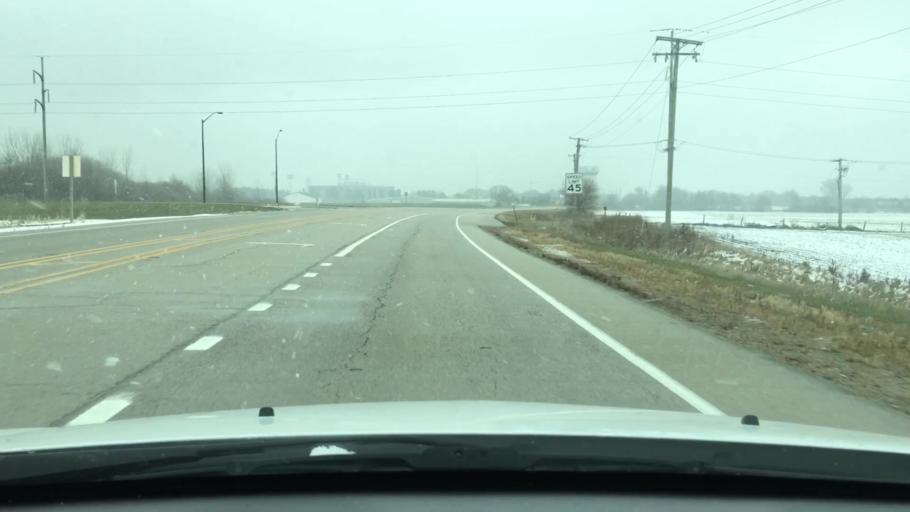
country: US
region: Illinois
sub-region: DeKalb County
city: DeKalb
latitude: 41.9332
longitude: -88.7939
